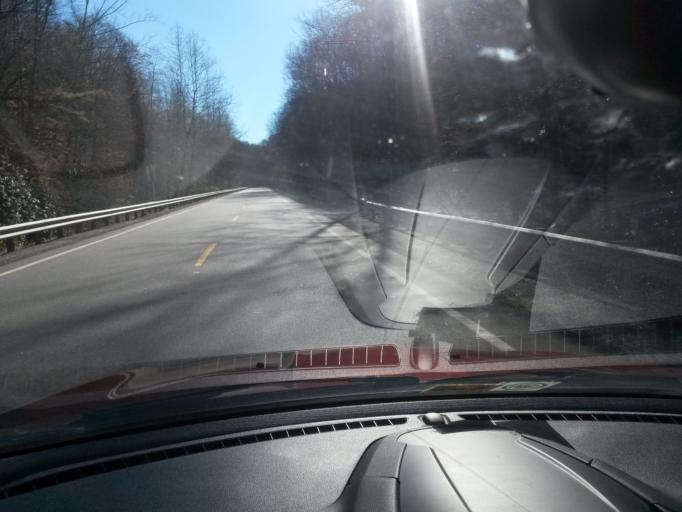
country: US
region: Virginia
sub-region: Henry County
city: Pannill Fork
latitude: 36.7772
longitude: -80.1201
